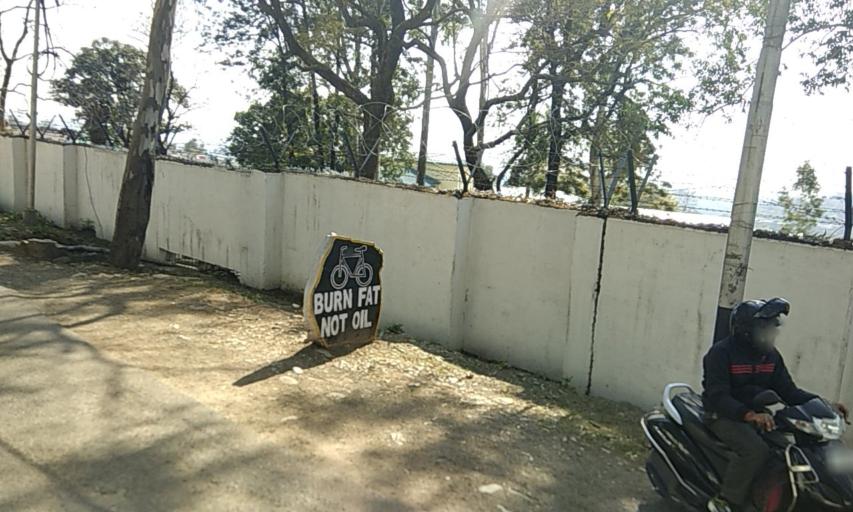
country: IN
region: Himachal Pradesh
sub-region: Kangra
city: Dharmsala
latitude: 32.1802
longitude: 76.3772
